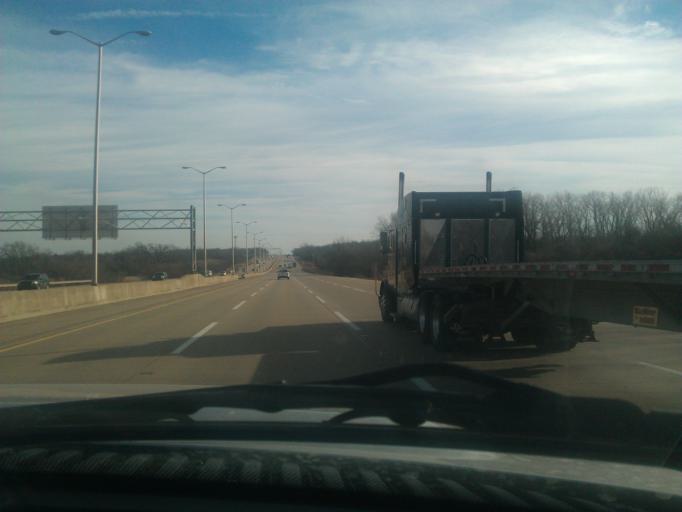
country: US
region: Illinois
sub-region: Lake County
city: Wadsworth
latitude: 42.4222
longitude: -87.9476
